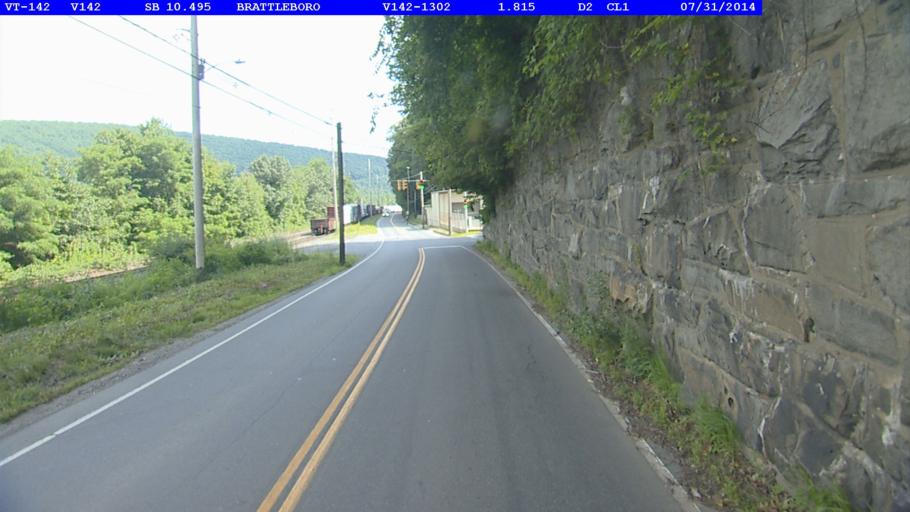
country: US
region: Vermont
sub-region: Windham County
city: Brattleboro
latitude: 42.8465
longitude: -72.5539
